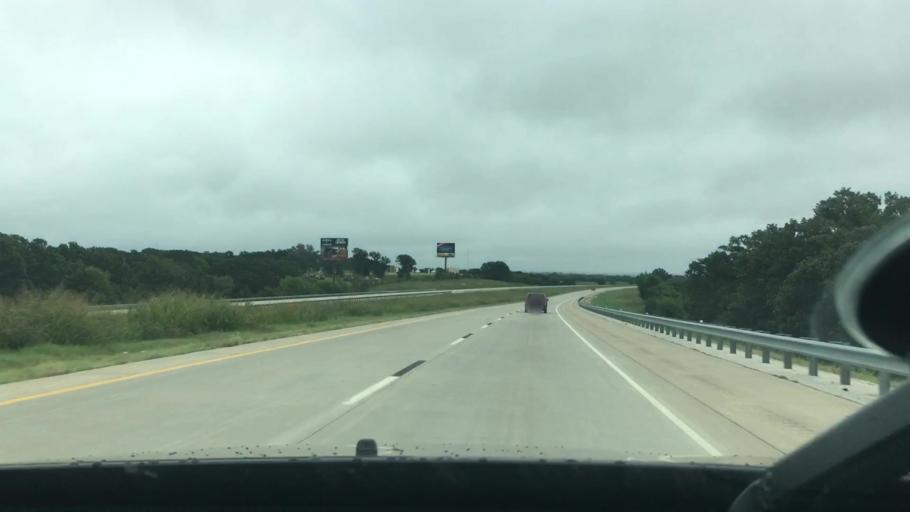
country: US
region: Oklahoma
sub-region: Okfuskee County
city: Boley
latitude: 35.3850
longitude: -96.5020
